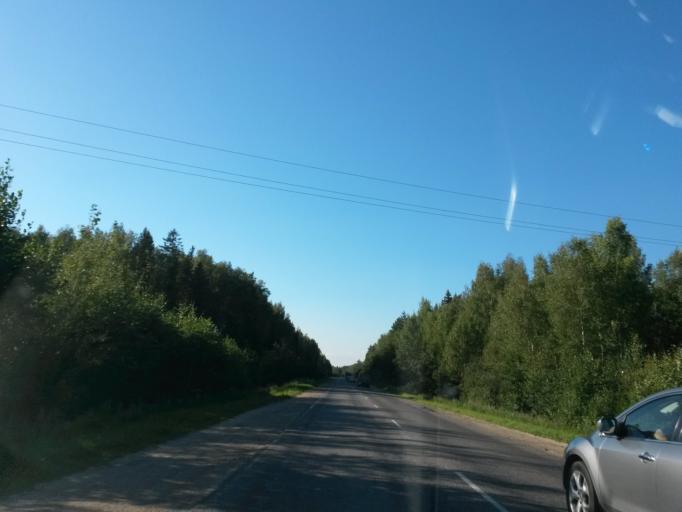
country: RU
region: Ivanovo
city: Novo-Talitsy
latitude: 57.0423
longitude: 40.7417
